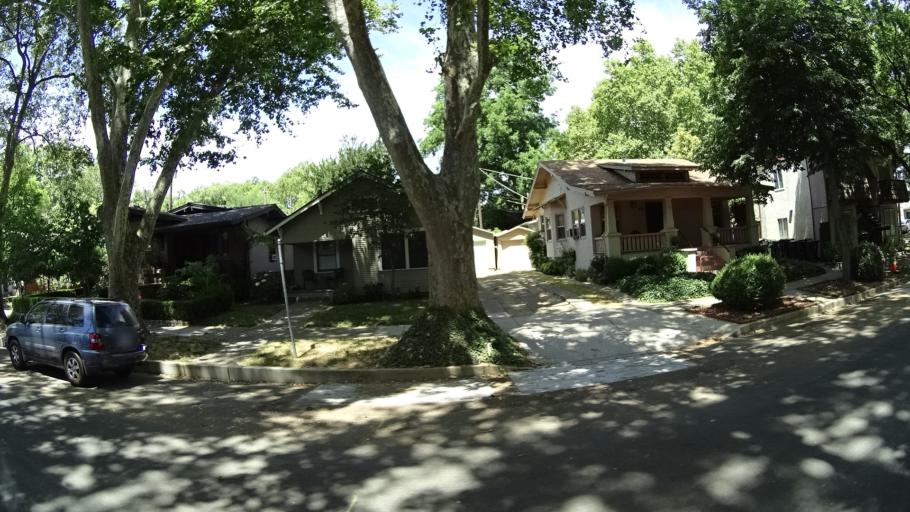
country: US
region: California
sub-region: Sacramento County
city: Sacramento
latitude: 38.5820
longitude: -121.4701
